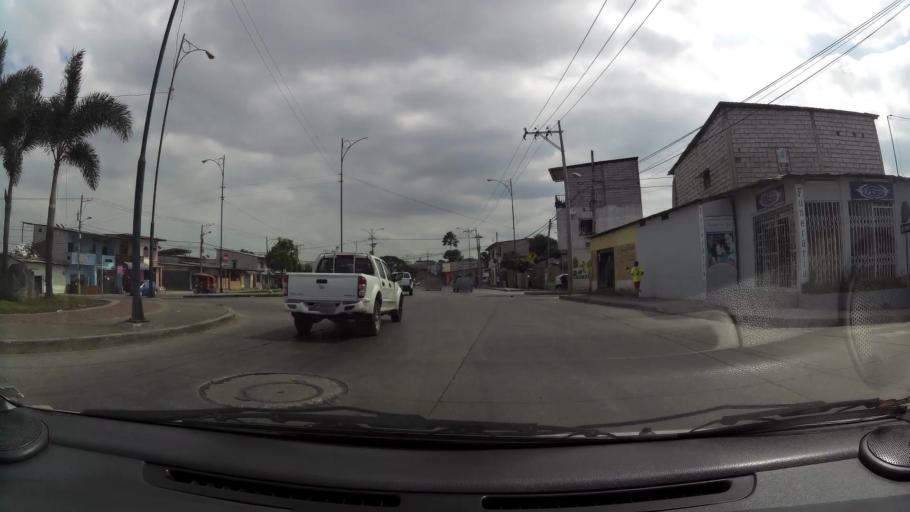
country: EC
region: Guayas
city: Santa Lucia
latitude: -2.0895
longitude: -79.9347
